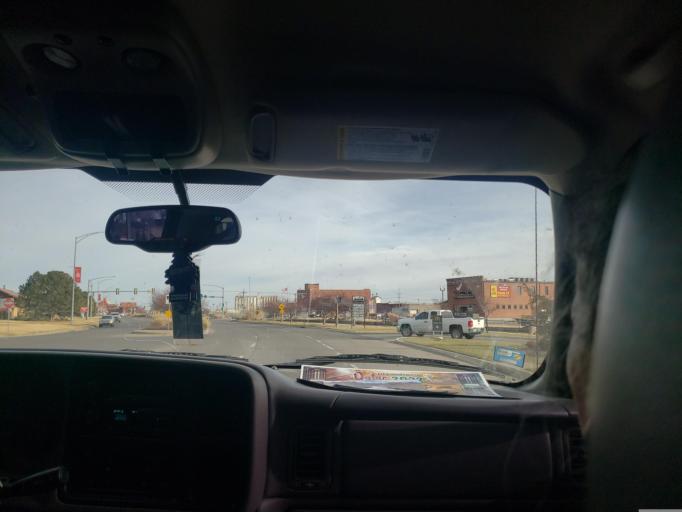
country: US
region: Kansas
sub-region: Ford County
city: Dodge City
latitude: 37.7529
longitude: -100.0230
